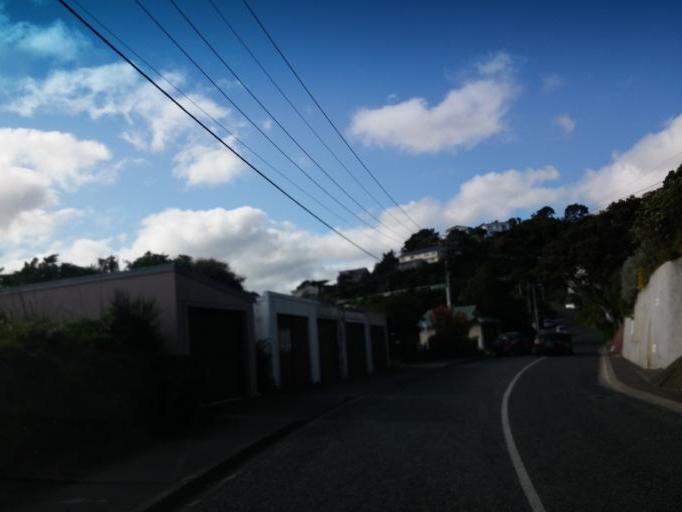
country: NZ
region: Wellington
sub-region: Wellington City
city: Wellington
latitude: -41.3192
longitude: 174.8210
